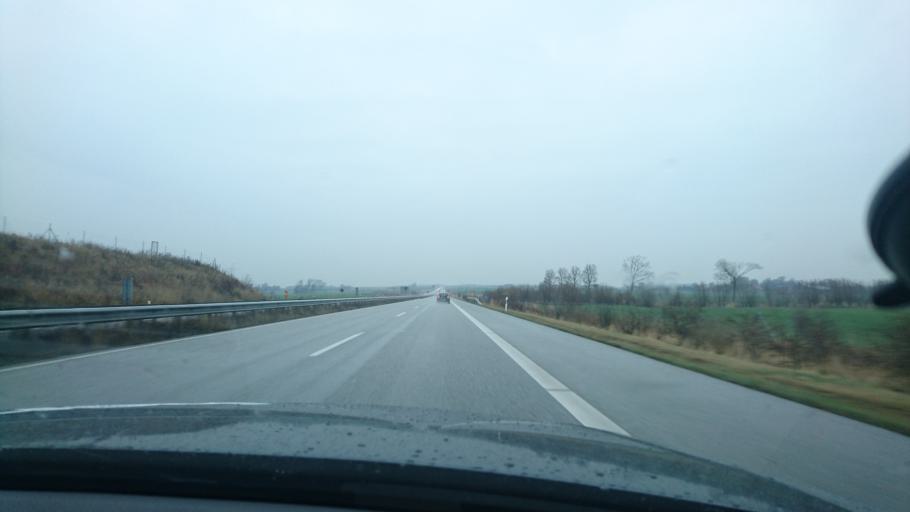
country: DE
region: Schleswig-Holstein
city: Gremersdorf
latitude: 54.3373
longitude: 10.9388
